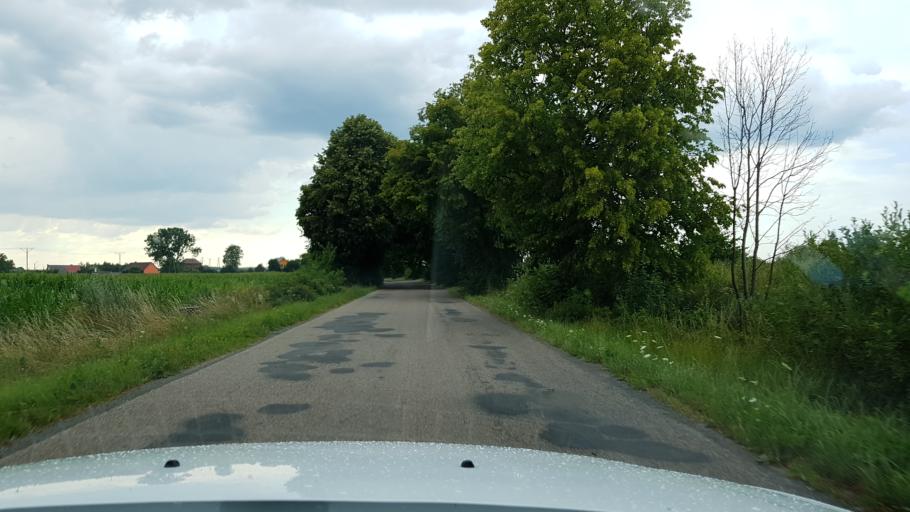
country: PL
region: West Pomeranian Voivodeship
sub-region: Powiat walecki
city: Walcz
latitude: 53.3492
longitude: 16.3696
